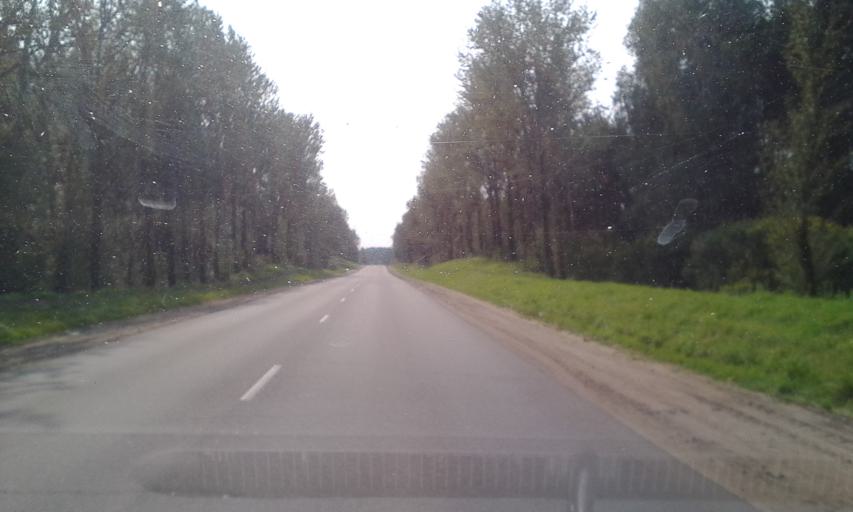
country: BY
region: Minsk
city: Hatava
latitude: 53.8123
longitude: 27.6471
